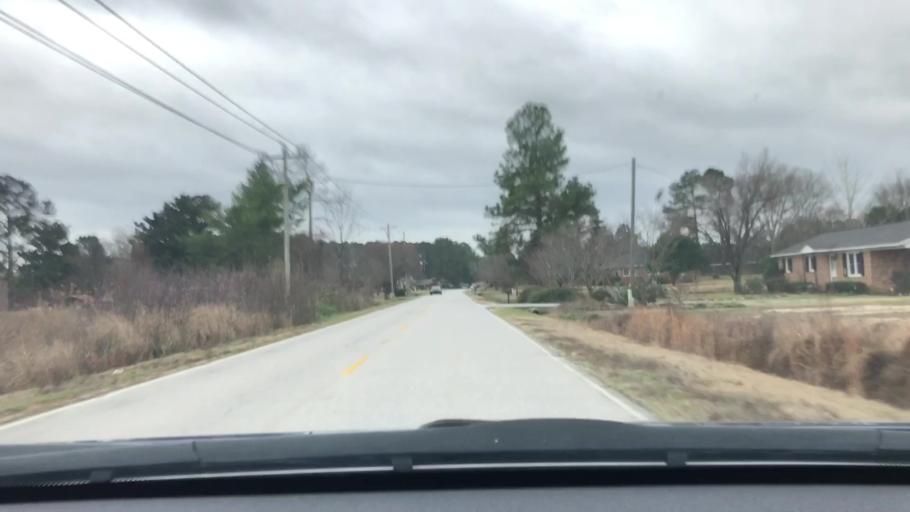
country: US
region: South Carolina
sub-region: Sumter County
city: Cane Savannah
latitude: 33.9214
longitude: -80.4052
